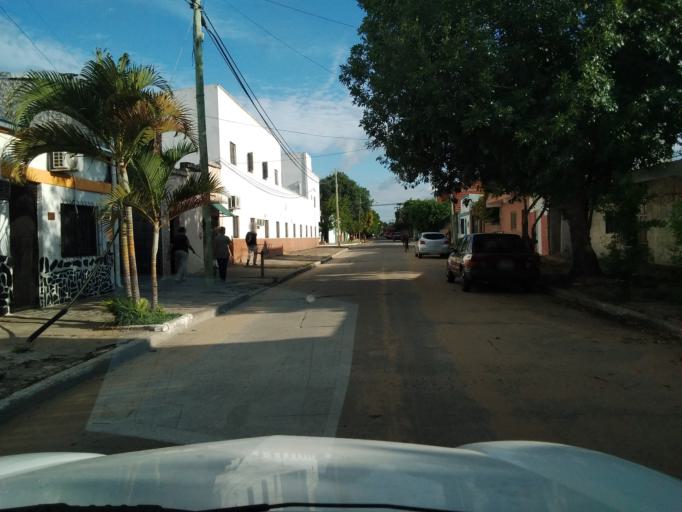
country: AR
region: Corrientes
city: Corrientes
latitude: -27.4619
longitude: -58.8192
